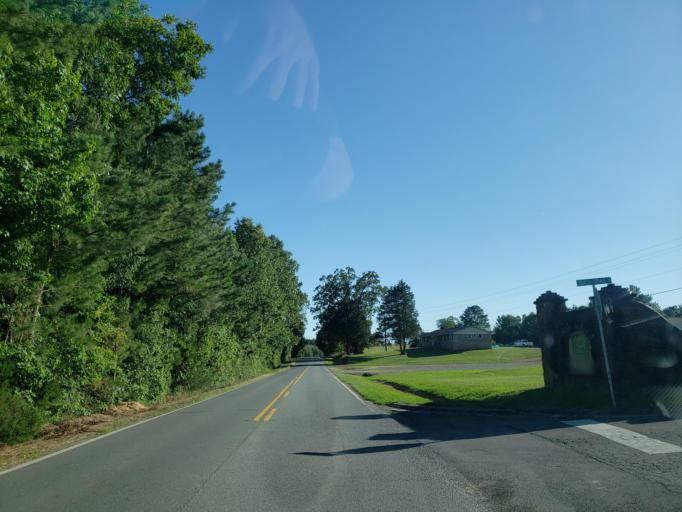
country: US
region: Georgia
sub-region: Floyd County
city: Shannon
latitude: 34.3658
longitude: -85.1342
